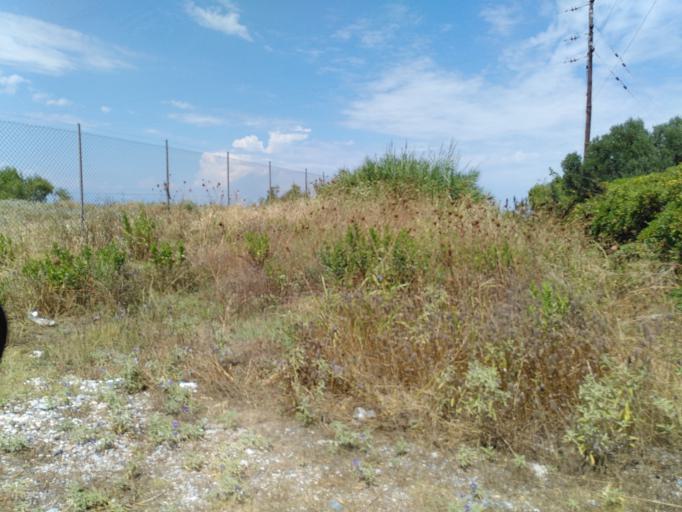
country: GR
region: Central Macedonia
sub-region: Nomos Thessalonikis
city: Agia Triada
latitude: 40.5054
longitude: 22.8454
